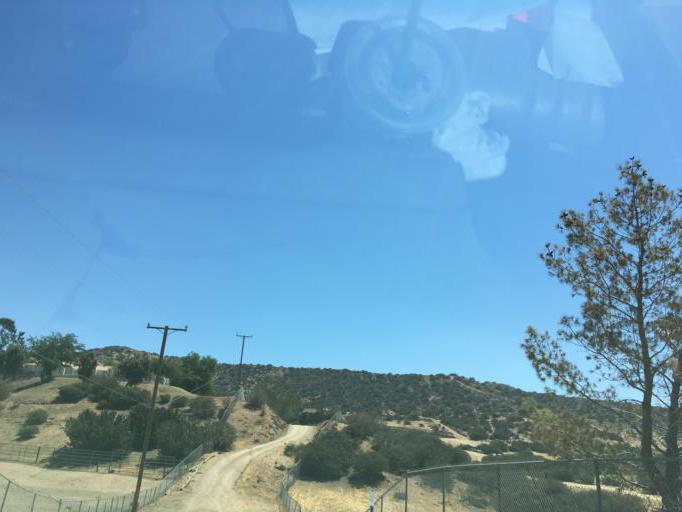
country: US
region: California
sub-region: Los Angeles County
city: Acton
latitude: 34.5244
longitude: -118.2244
